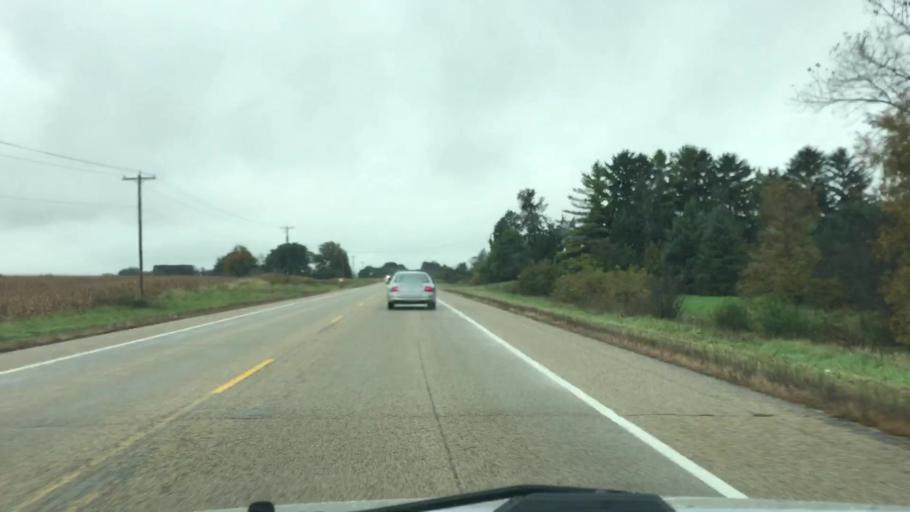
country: US
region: Wisconsin
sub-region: Jefferson County
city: Palmyra
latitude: 42.8677
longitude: -88.6468
